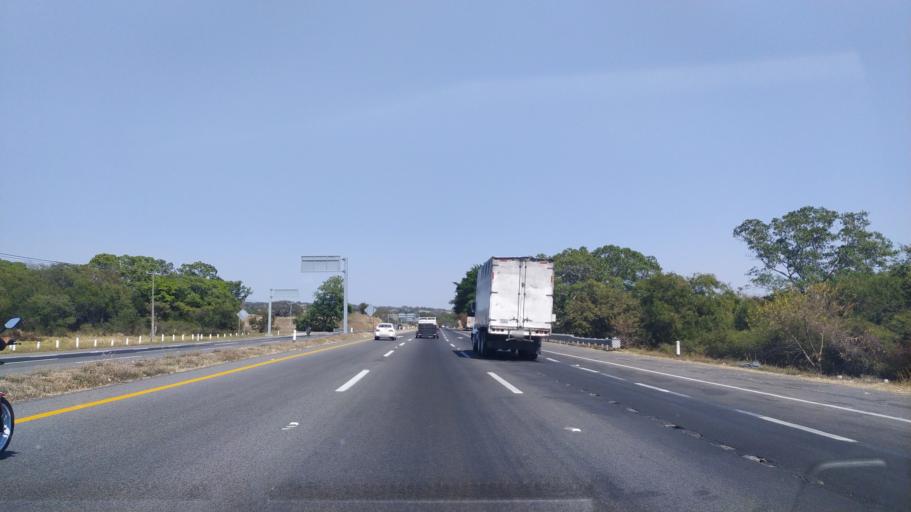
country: MX
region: Colima
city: Cuauhtemoc
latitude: 19.3130
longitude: -103.6013
